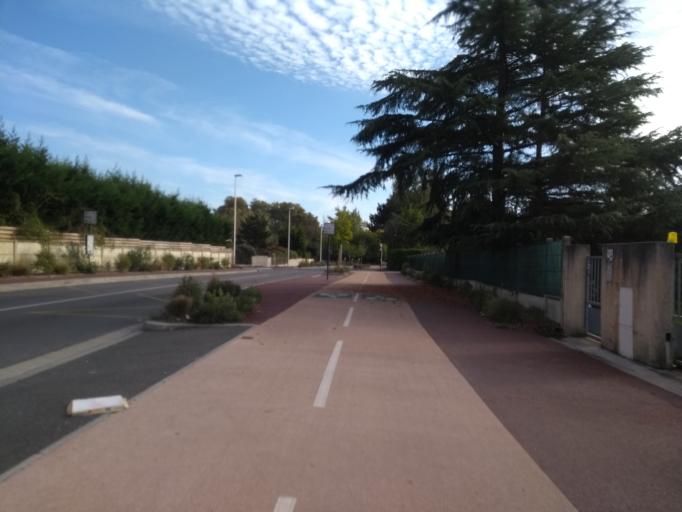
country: FR
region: Aquitaine
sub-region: Departement de la Gironde
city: Gradignan
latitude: 44.7689
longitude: -0.6205
